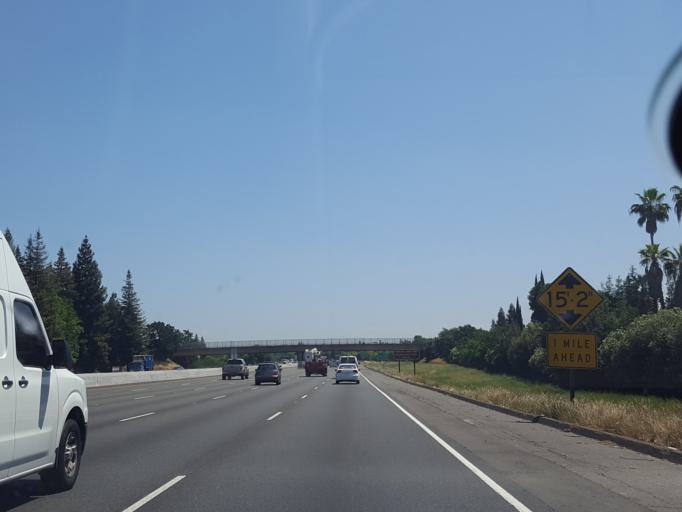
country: US
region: California
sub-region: Sacramento County
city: La Riviera
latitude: 38.5613
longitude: -121.3534
